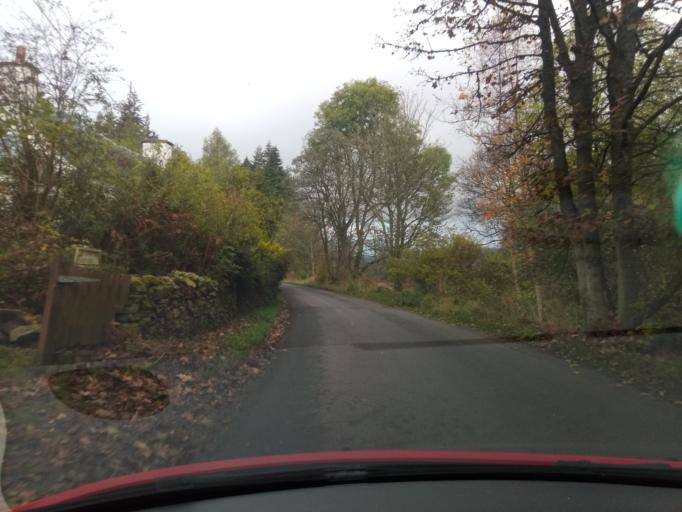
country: GB
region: Scotland
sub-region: The Scottish Borders
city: Innerleithen
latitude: 55.6207
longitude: -3.0917
